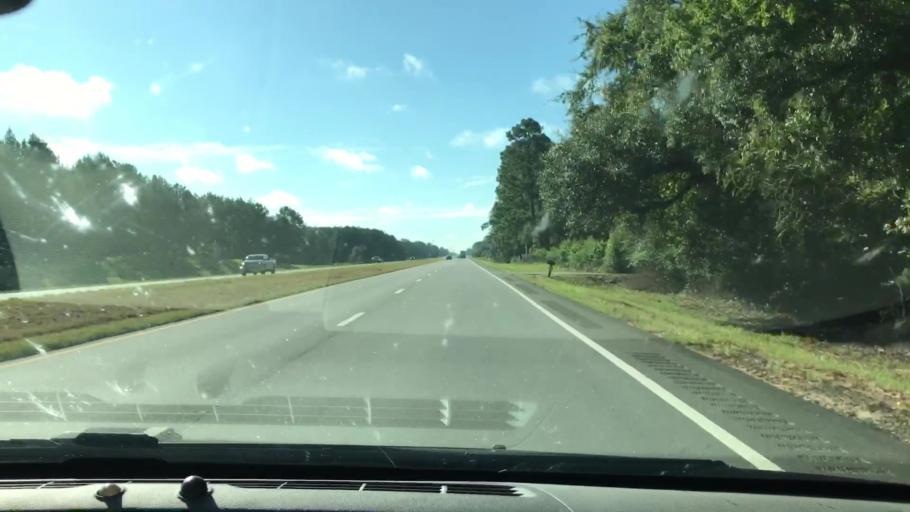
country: US
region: Georgia
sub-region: Lee County
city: Leesburg
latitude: 31.6780
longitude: -84.2972
